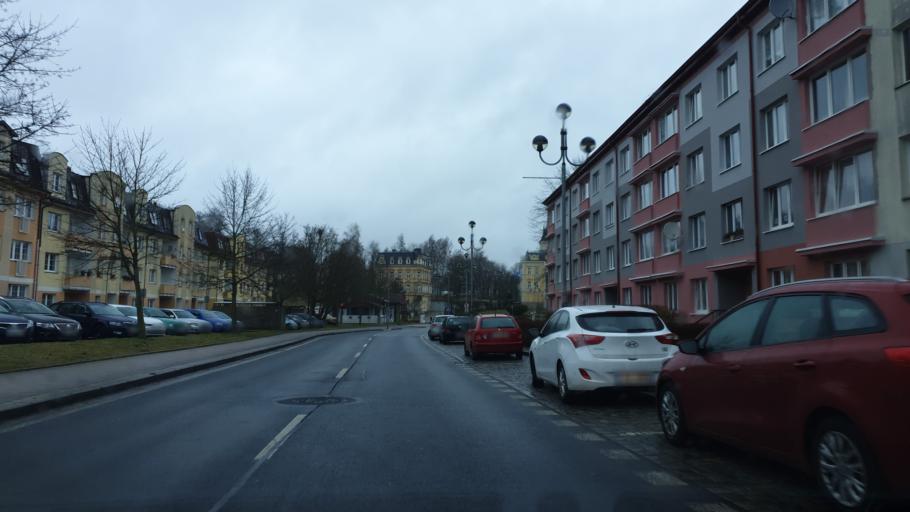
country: CZ
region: Karlovarsky
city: As
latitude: 50.2237
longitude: 12.1866
